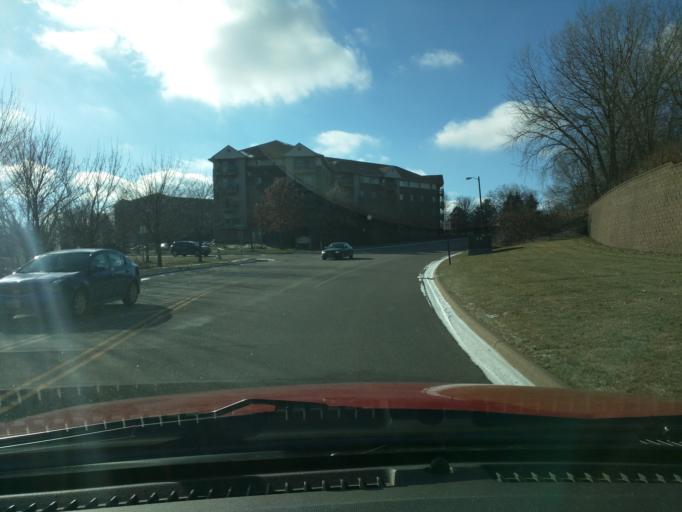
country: US
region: Minnesota
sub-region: Hennepin County
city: Eden Prairie
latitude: 44.8671
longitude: -93.4130
